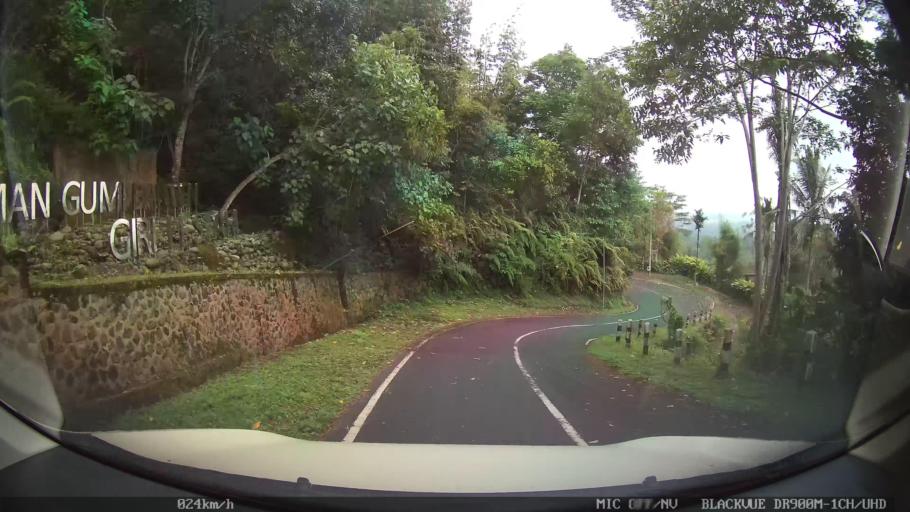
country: ID
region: Bali
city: Peneng
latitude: -8.3698
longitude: 115.2142
